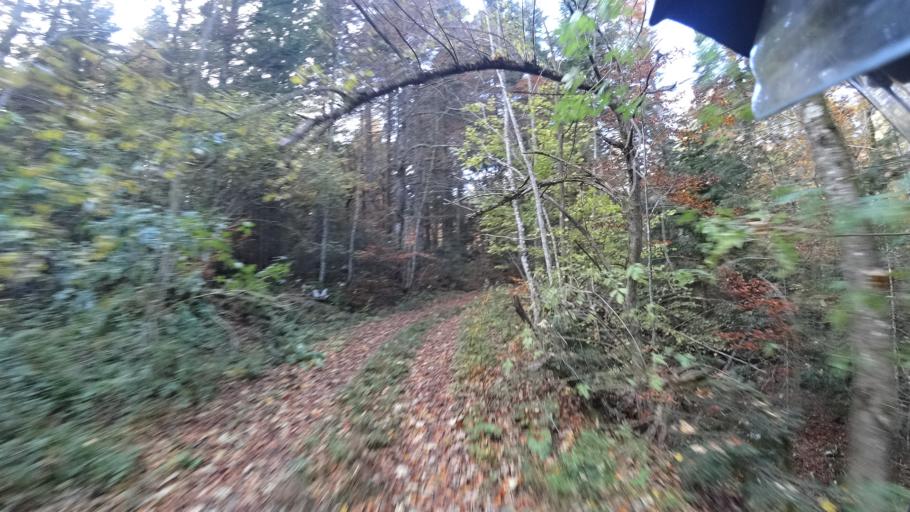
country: HR
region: Karlovacka
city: Plaski
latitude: 45.0370
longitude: 15.3231
